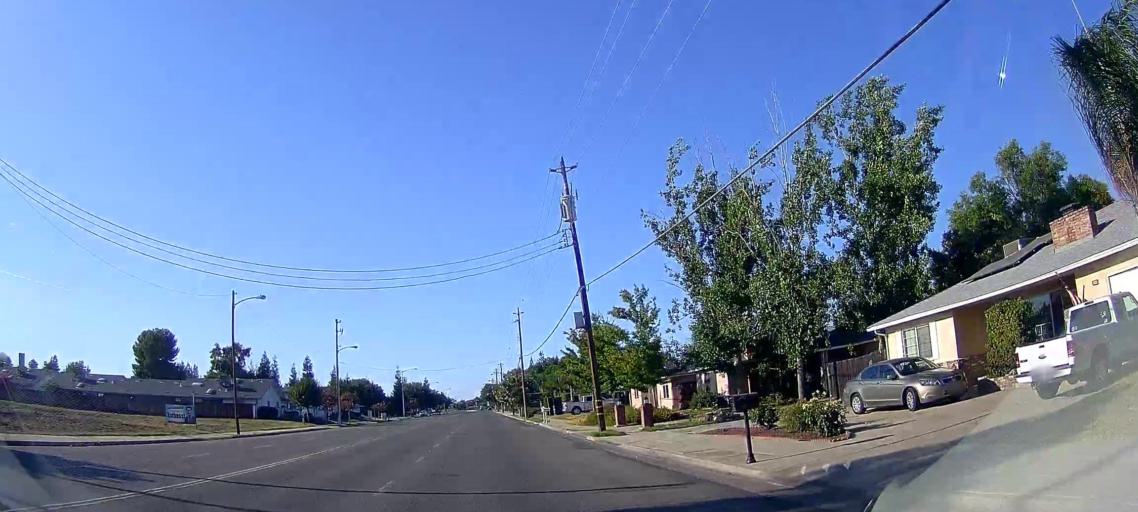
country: US
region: California
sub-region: Fresno County
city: Fresno
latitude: 36.8328
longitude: -119.7993
